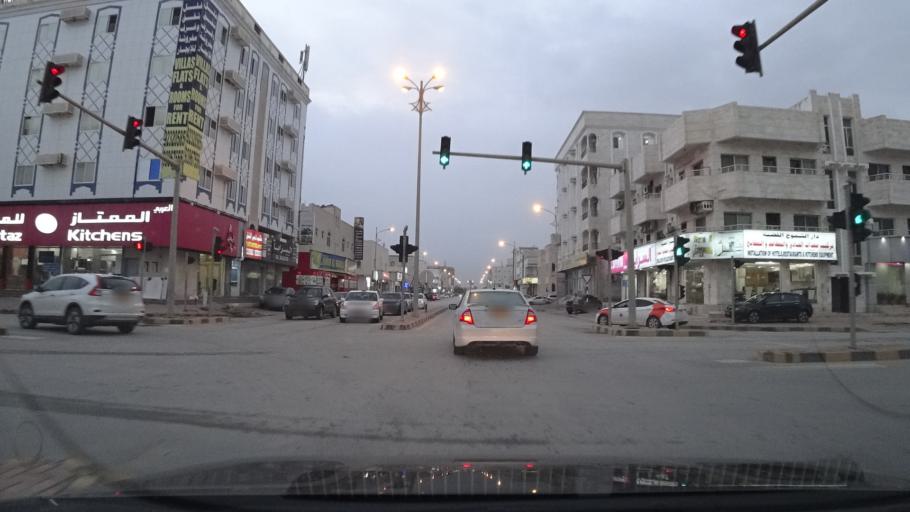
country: OM
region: Zufar
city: Salalah
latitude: 17.0174
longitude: 54.0849
